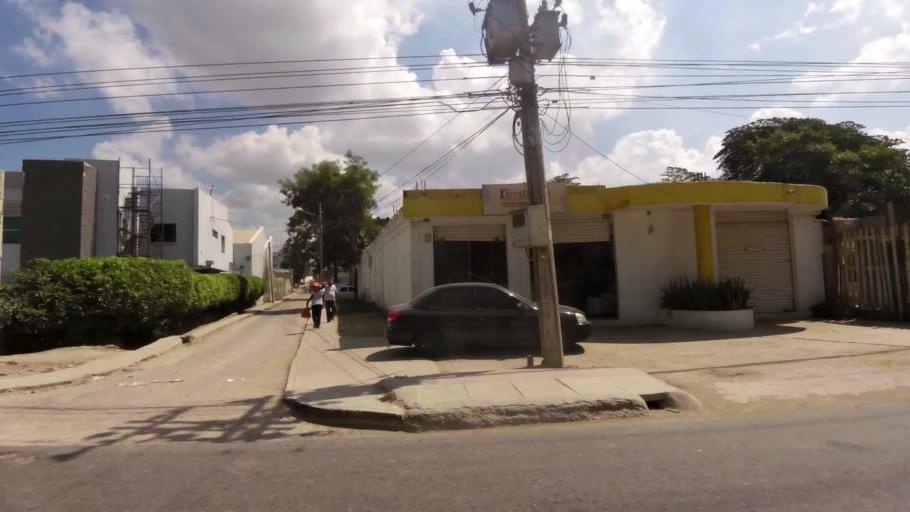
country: CO
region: Bolivar
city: Cartagena
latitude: 10.3703
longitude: -75.5061
